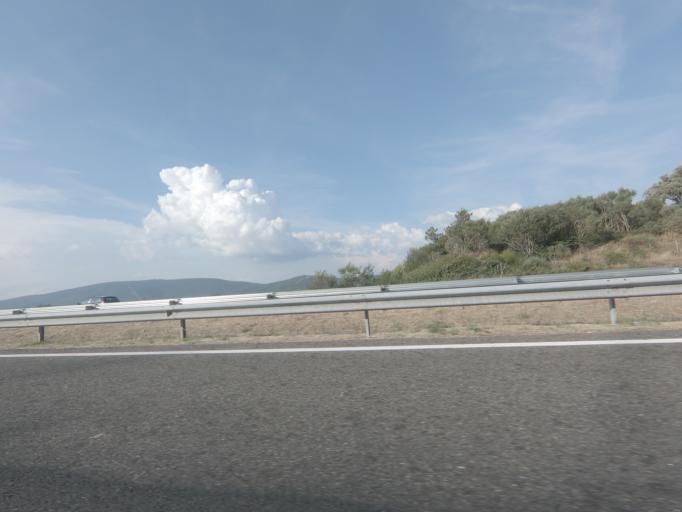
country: ES
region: Galicia
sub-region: Provincia de Ourense
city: Verin
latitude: 41.9603
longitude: -7.5150
